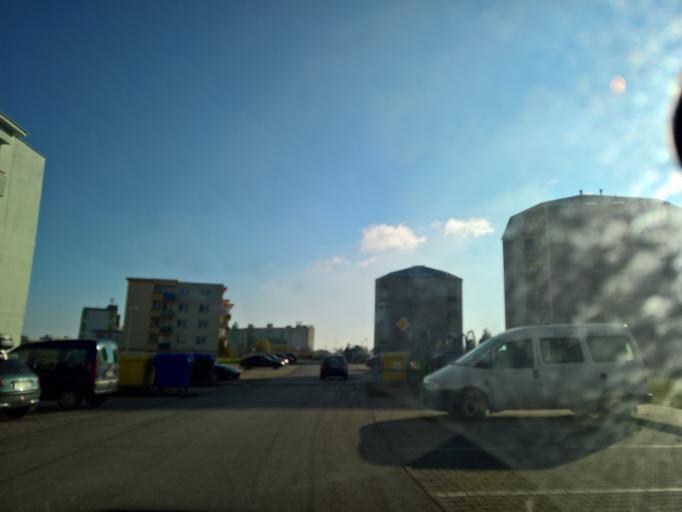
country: SK
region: Nitriansky
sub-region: Okres Nitra
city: Nitra
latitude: 48.3078
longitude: 18.0459
